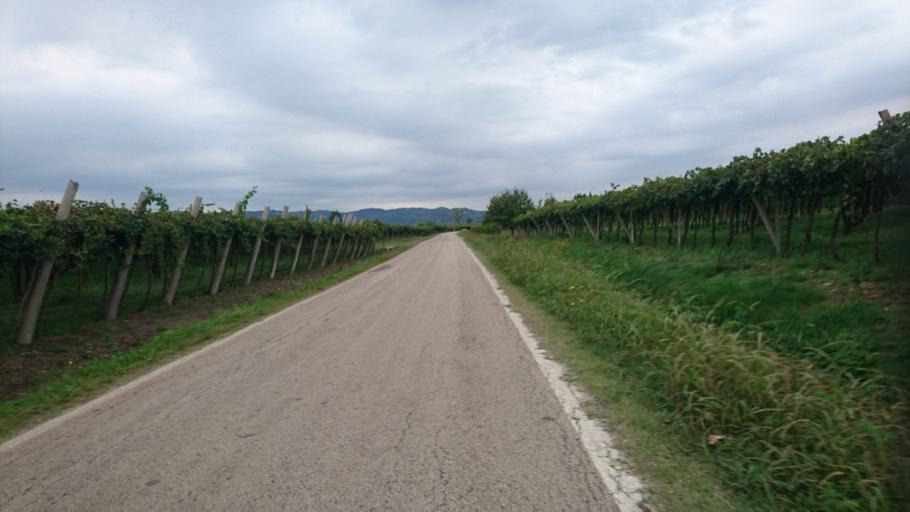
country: IT
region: Veneto
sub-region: Provincia di Verona
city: Locara
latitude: 45.4259
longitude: 11.3141
